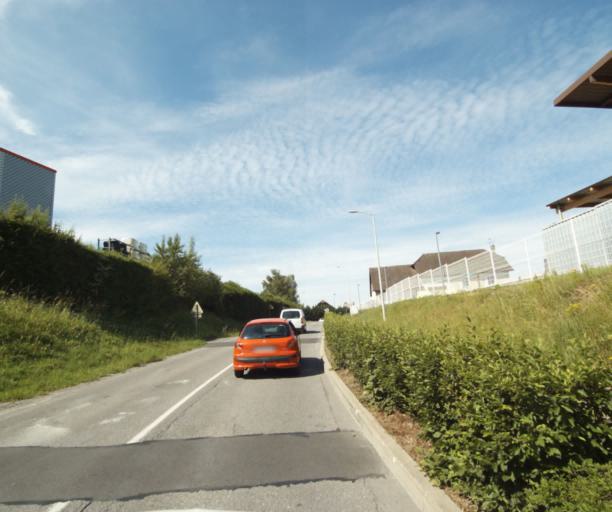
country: FR
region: Rhone-Alpes
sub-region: Departement de la Haute-Savoie
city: Anthy-sur-Leman
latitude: 46.3437
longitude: 6.4160
